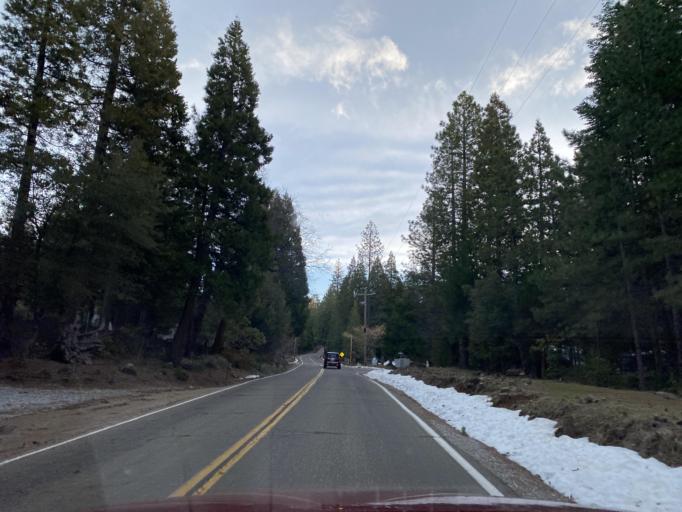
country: US
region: California
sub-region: Amador County
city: Pioneer
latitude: 38.4977
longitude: -120.5631
